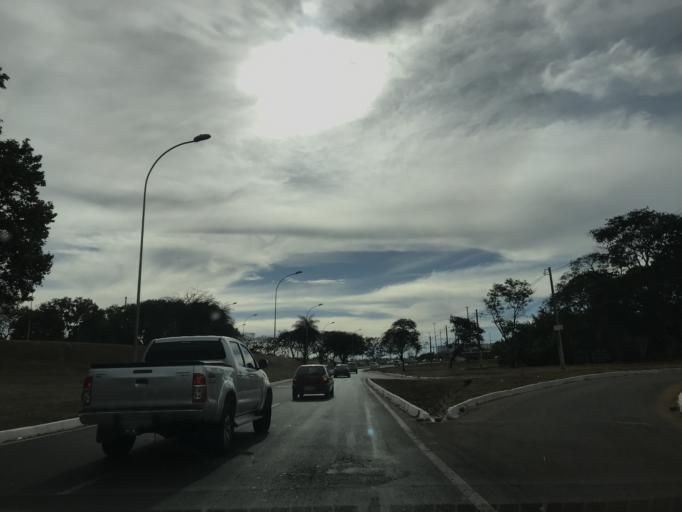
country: BR
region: Federal District
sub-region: Brasilia
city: Brasilia
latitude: -15.8402
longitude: -47.9513
